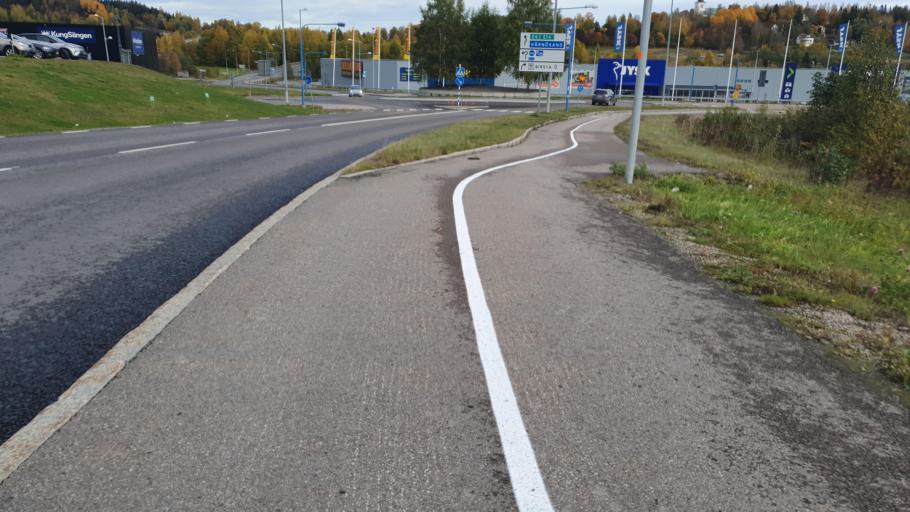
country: SE
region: Vaesternorrland
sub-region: Sundsvalls Kommun
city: Sundsbruk
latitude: 62.4429
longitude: 17.3406
